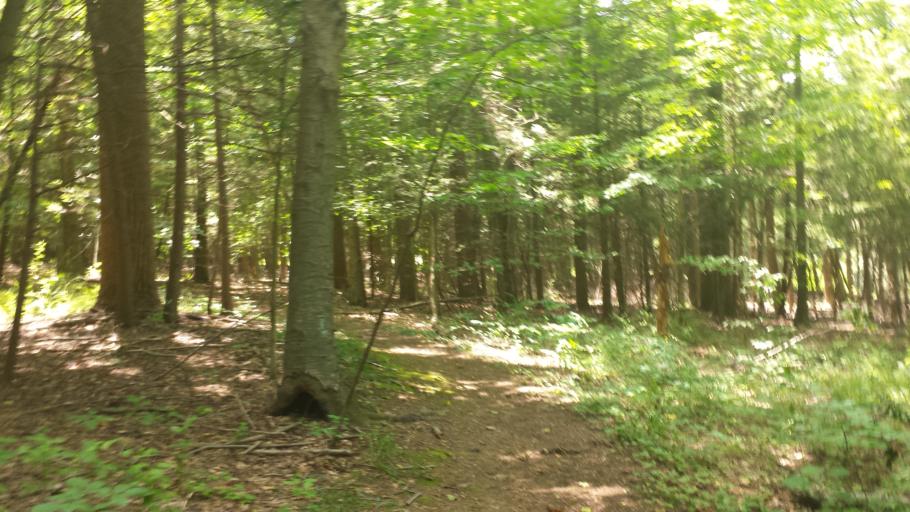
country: US
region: New York
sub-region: Westchester County
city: Yorktown Heights
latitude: 41.2283
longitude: -73.7911
